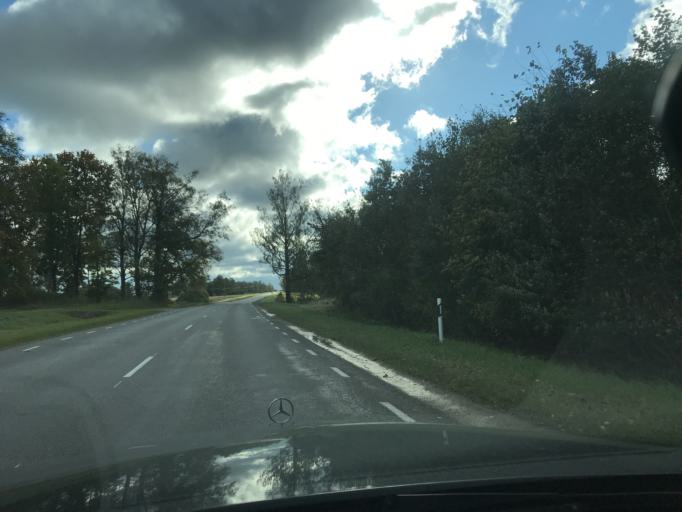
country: EE
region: Vorumaa
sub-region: Antsla vald
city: Vana-Antsla
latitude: 57.9406
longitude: 26.3077
